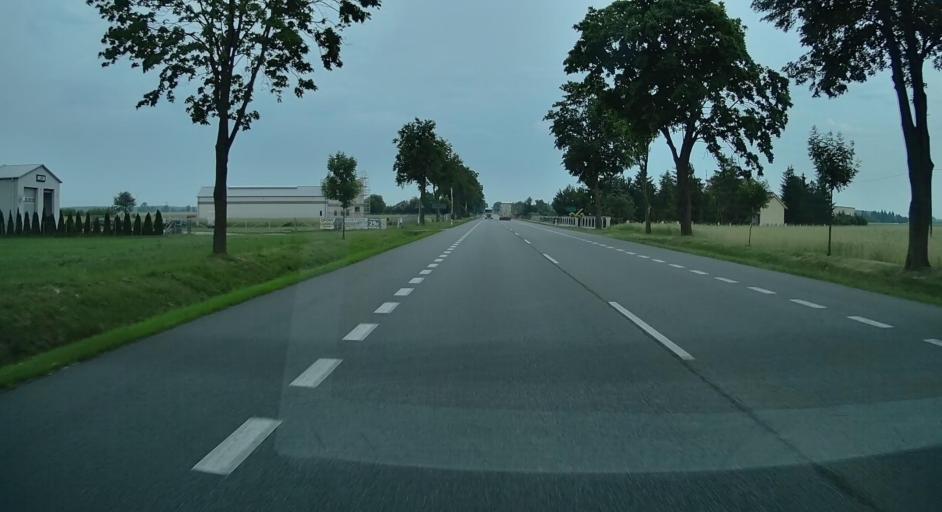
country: PL
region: Masovian Voivodeship
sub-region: Powiat siedlecki
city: Zbuczyn
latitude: 52.1110
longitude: 22.3799
